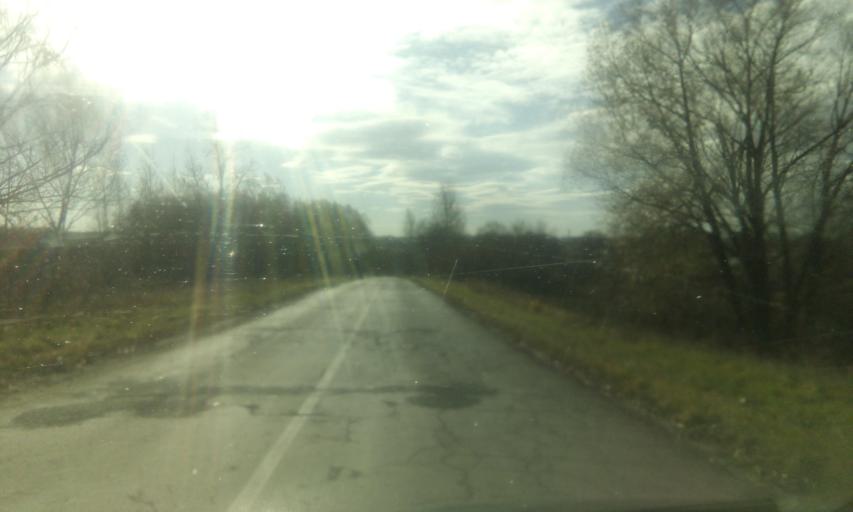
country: RU
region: Tula
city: Dubovka
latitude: 53.9521
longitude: 38.0295
